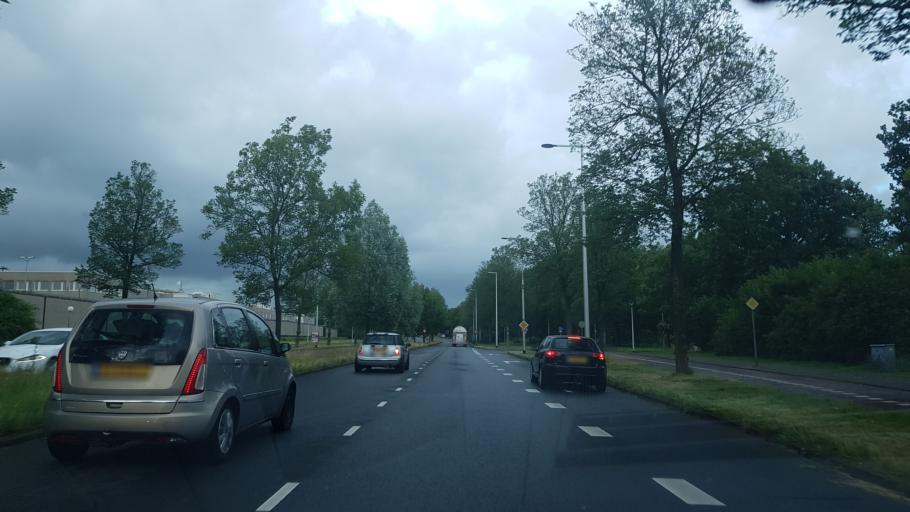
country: NL
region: Friesland
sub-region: Gemeente Leeuwarden
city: Huizum
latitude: 53.1917
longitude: 5.8299
